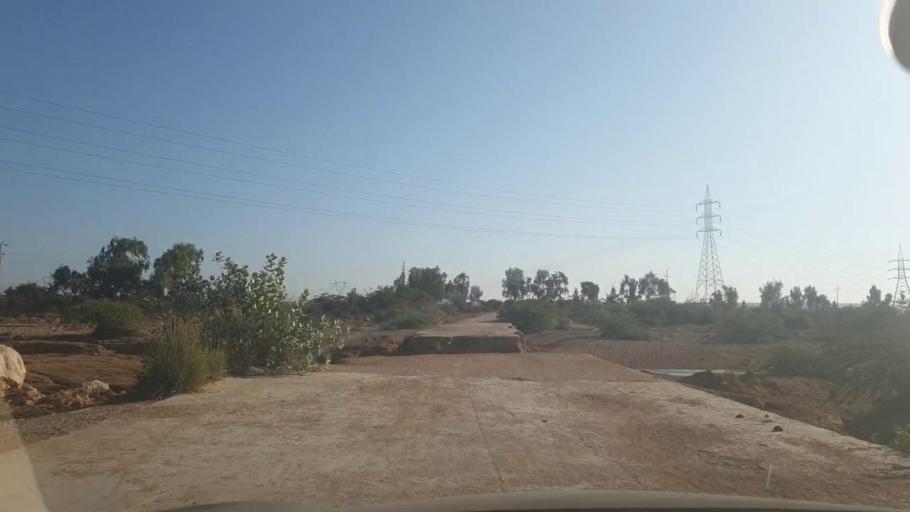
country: PK
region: Sindh
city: Malir Cantonment
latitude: 25.1194
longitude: 67.2838
